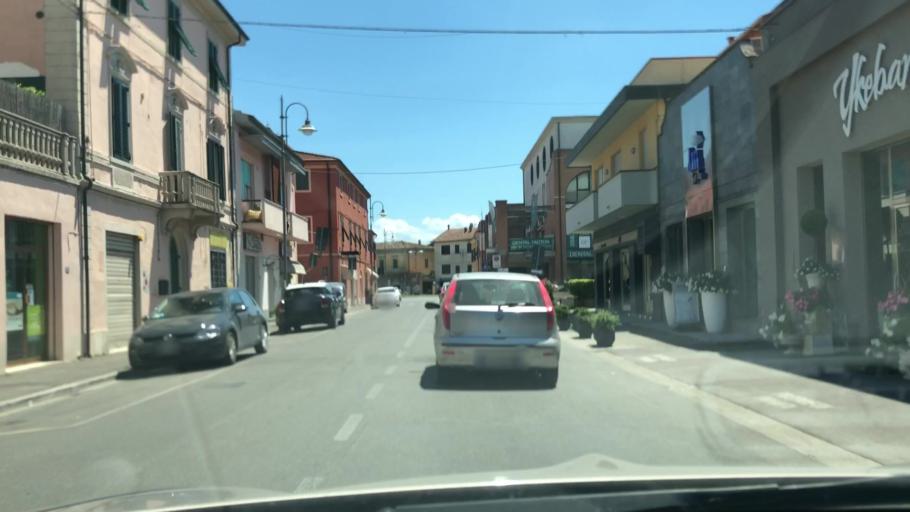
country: IT
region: Tuscany
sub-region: Province of Pisa
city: Ponsacco
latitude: 43.6223
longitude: 10.6299
